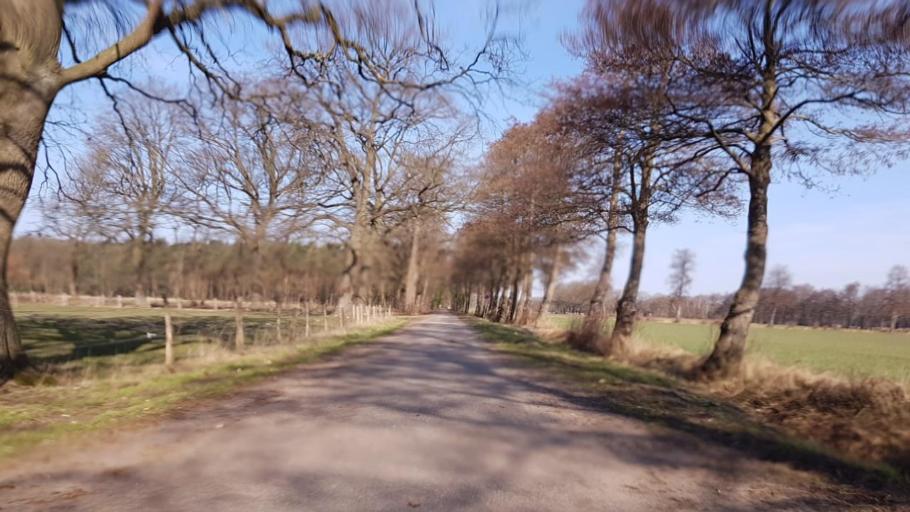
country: DE
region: Lower Saxony
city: Garbsen-Mitte
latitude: 52.4505
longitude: 9.6377
